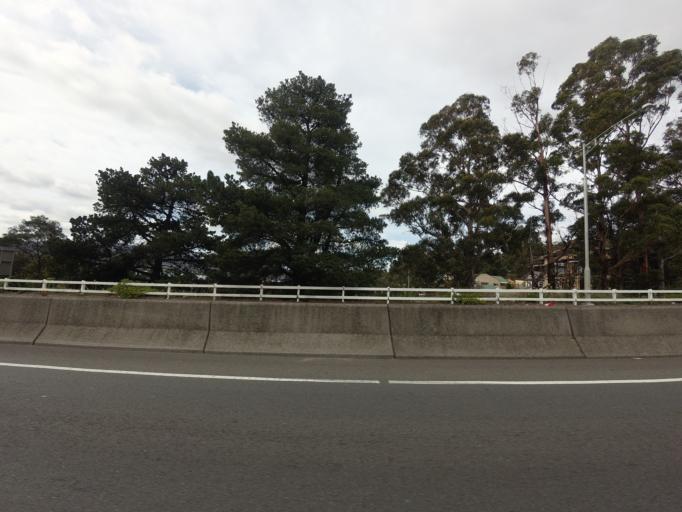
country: AU
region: Tasmania
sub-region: Hobart
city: New Town
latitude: -42.8557
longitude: 147.3166
